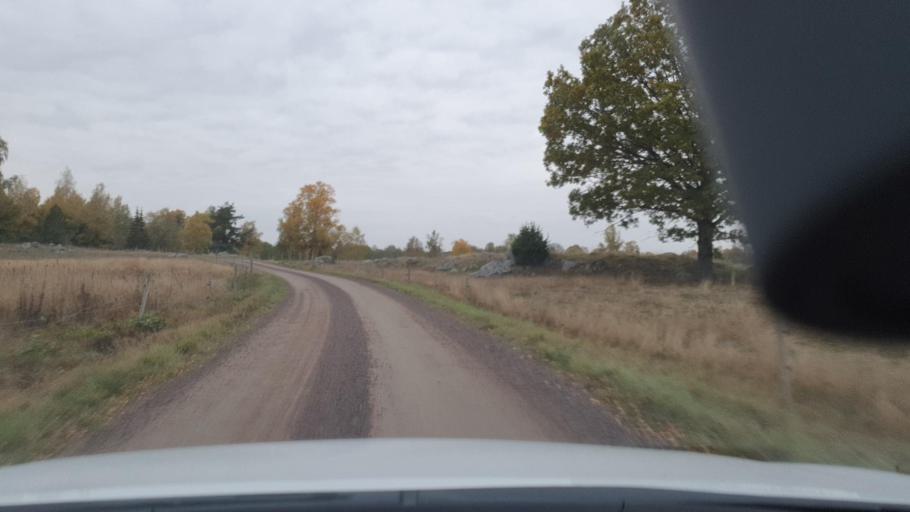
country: SE
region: Kalmar
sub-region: Hultsfreds Kommun
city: Malilla
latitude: 57.3189
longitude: 15.8111
